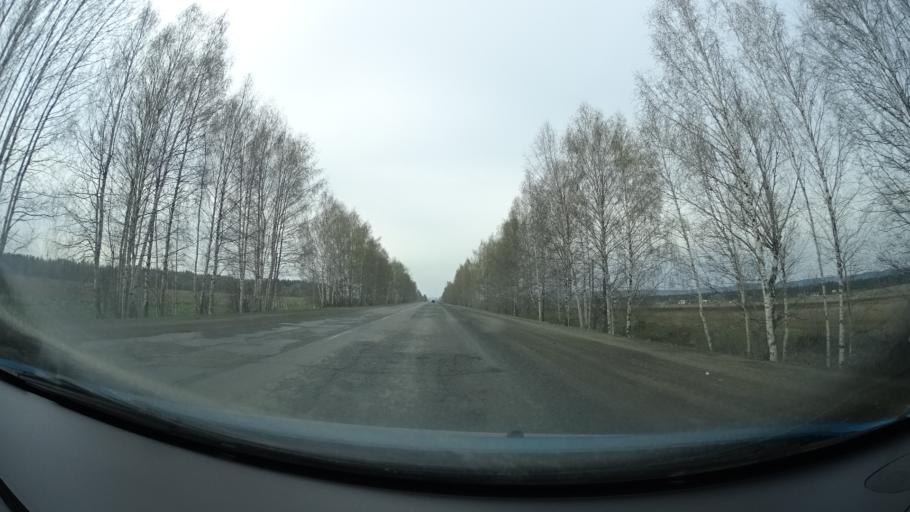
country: RU
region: Perm
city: Ust'-Kachka
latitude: 58.0544
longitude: 55.6005
